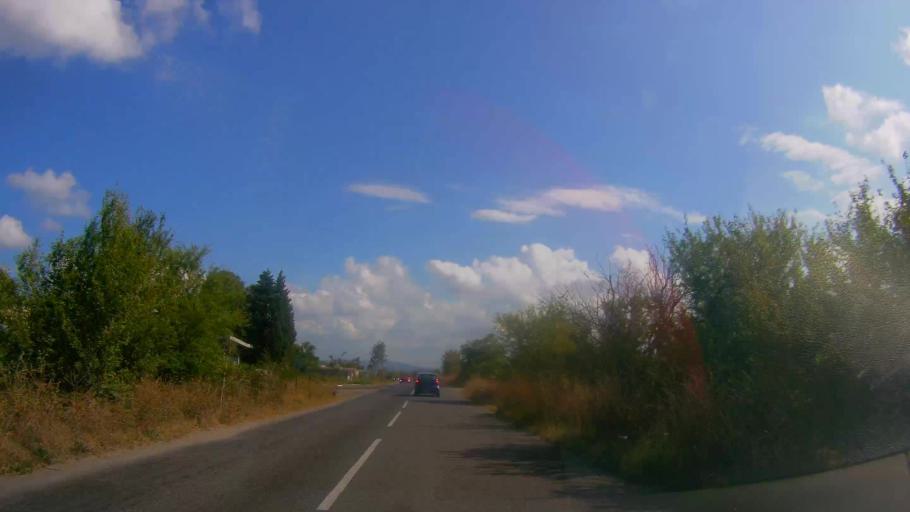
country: BG
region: Burgas
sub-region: Obshtina Burgas
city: Burgas
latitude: 42.4749
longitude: 27.4170
